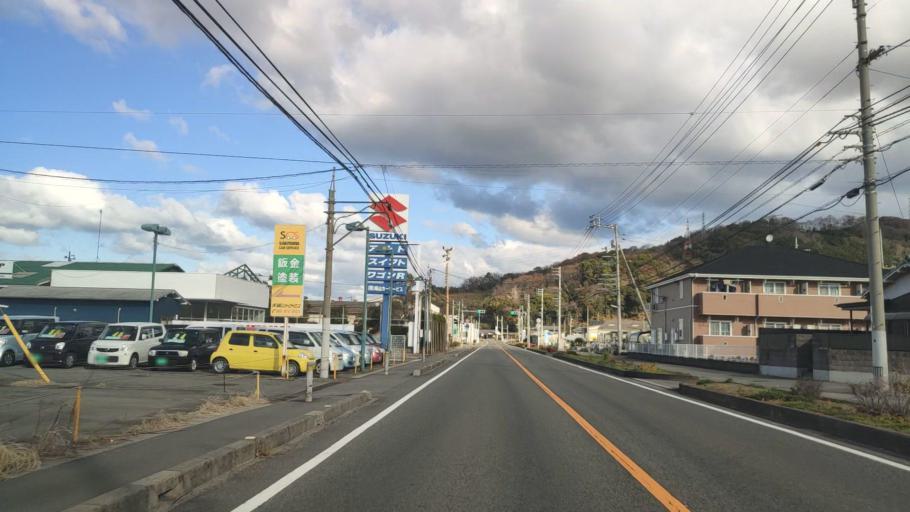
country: JP
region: Ehime
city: Masaki-cho
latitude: 33.8373
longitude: 132.7092
